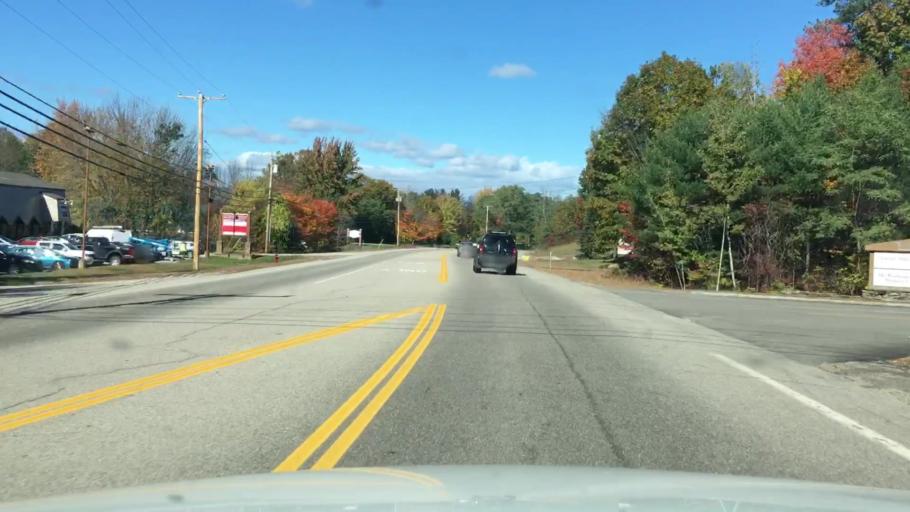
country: US
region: New Hampshire
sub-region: Carroll County
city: Conway
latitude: 43.9911
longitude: -71.1102
